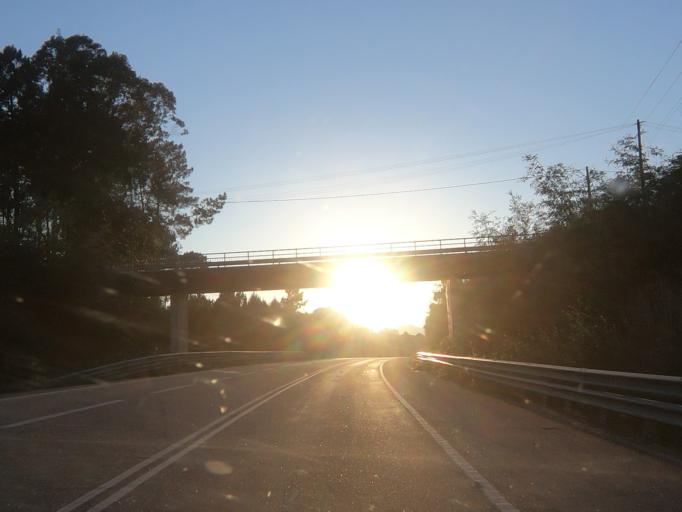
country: PT
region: Viseu
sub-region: Viseu
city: Rio de Loba
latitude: 40.6762
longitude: -7.8699
